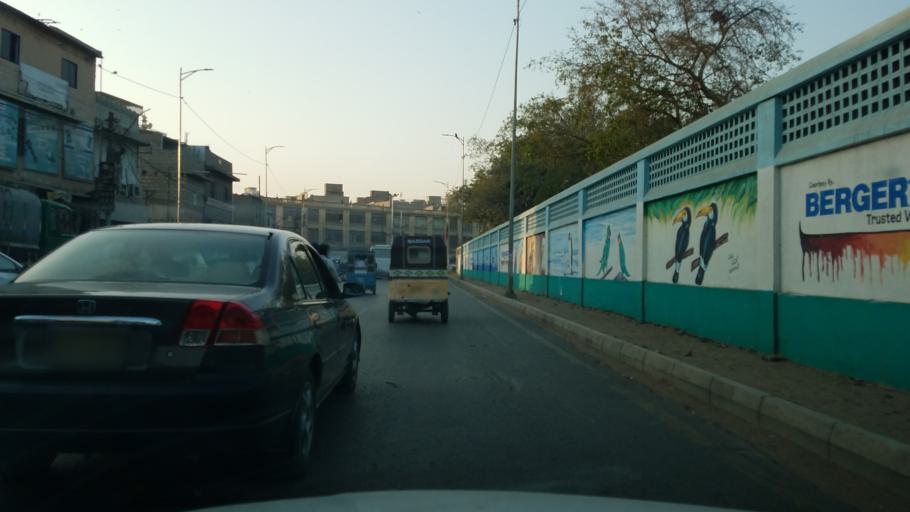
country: PK
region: Sindh
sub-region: Karachi District
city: Karachi
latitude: 24.8749
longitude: 67.0215
